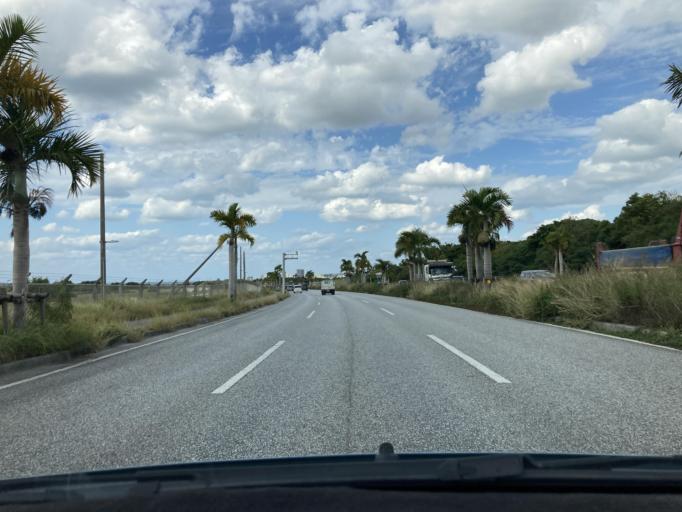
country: JP
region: Okinawa
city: Chatan
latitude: 26.3382
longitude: 127.7511
